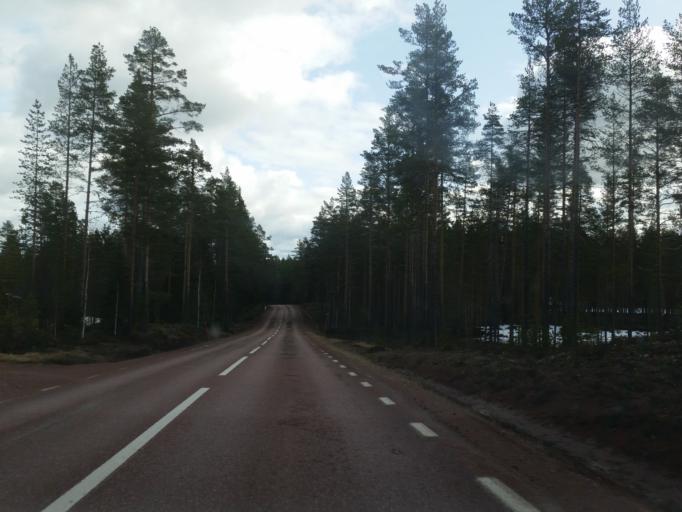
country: SE
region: Dalarna
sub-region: Alvdalens Kommun
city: AElvdalen
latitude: 61.3107
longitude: 13.6874
